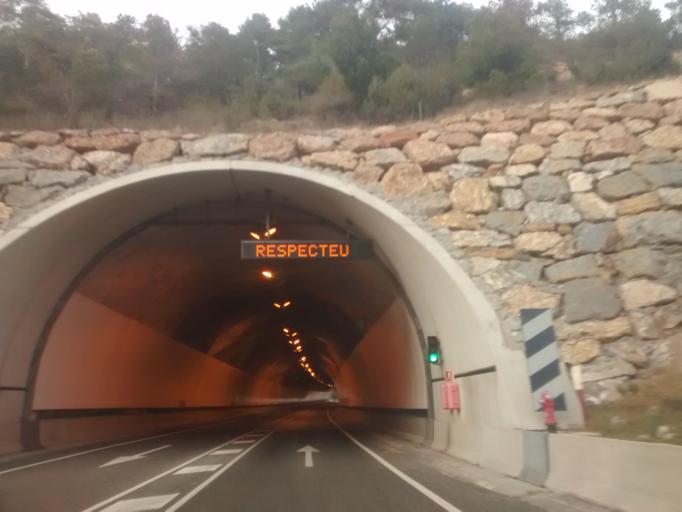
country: ES
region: Catalonia
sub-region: Provincia de Lleida
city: Coll de Nargo
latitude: 42.1448
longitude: 1.3072
